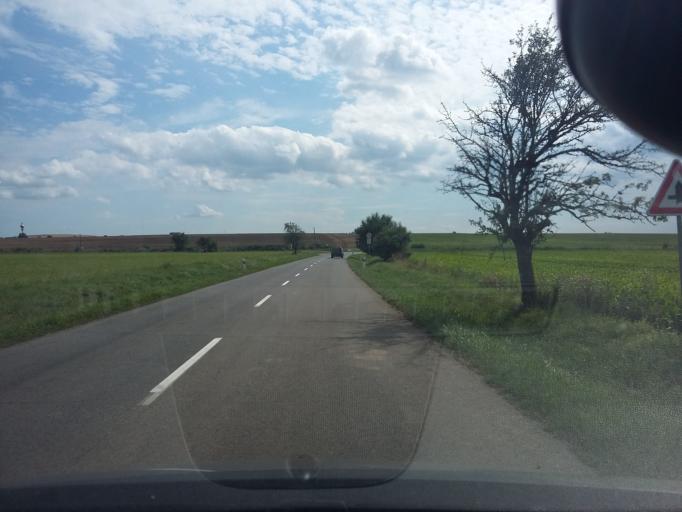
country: SK
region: Trnavsky
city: Gbely
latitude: 48.7362
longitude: 17.1670
